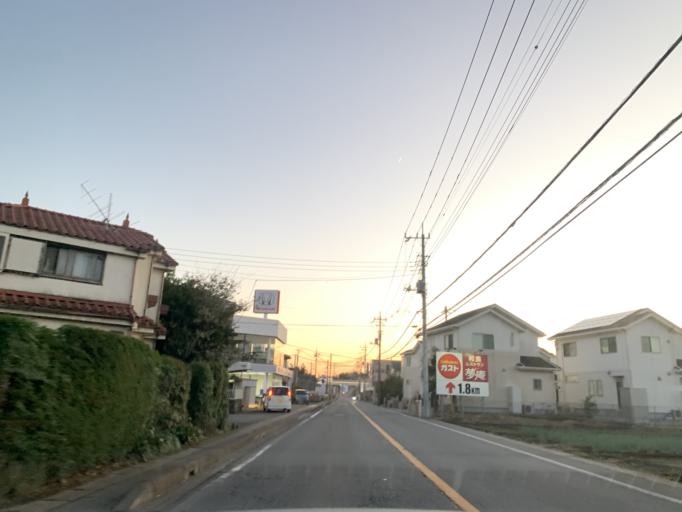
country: JP
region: Chiba
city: Nagareyama
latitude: 35.9073
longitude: 139.9032
